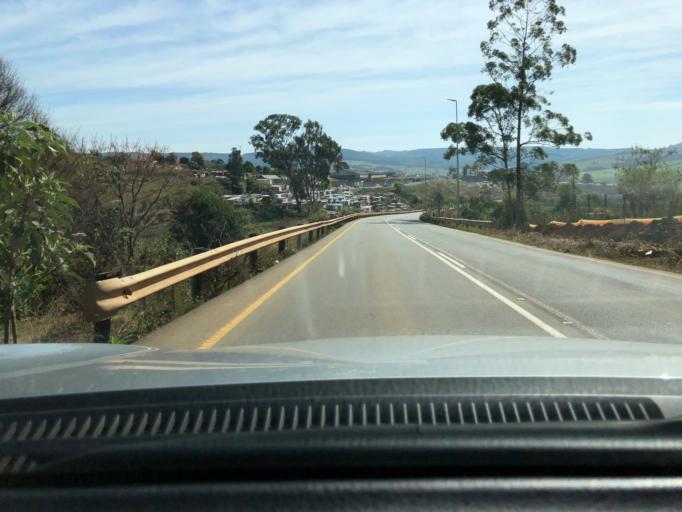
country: ZA
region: KwaZulu-Natal
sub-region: Sisonke District Municipality
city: Ixopo
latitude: -30.1541
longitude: 30.0654
